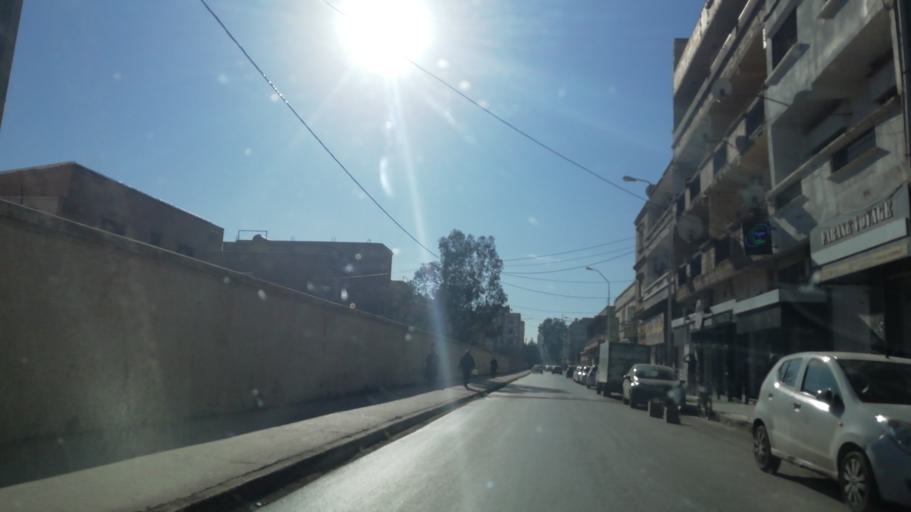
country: DZ
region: Oran
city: Oran
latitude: 35.6725
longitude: -0.6516
